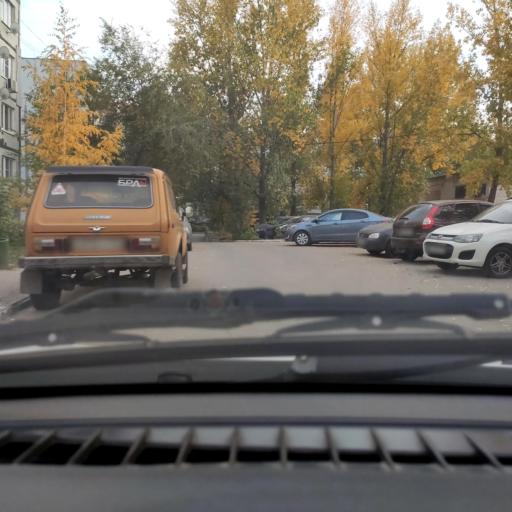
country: RU
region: Samara
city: Zhigulevsk
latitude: 53.4762
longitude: 49.5159
